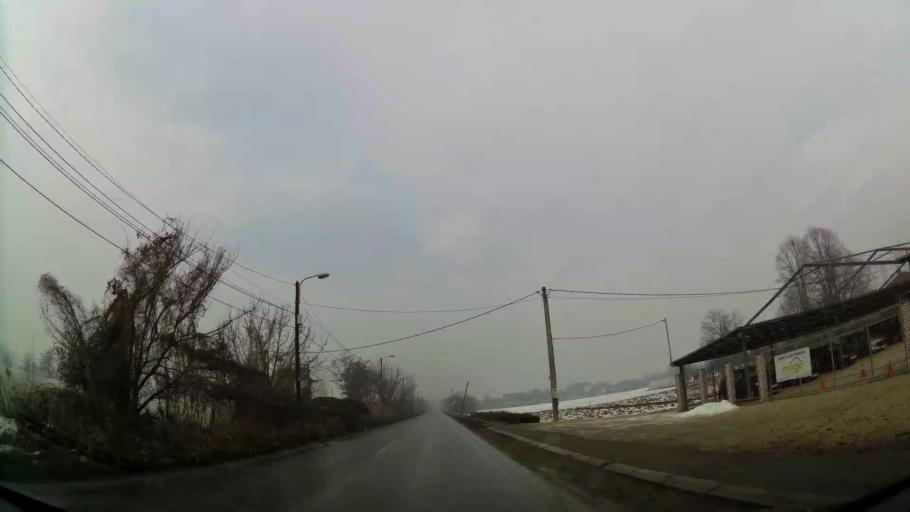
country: MK
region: Ilinden
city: Jurumleri
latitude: 41.9672
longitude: 21.5499
